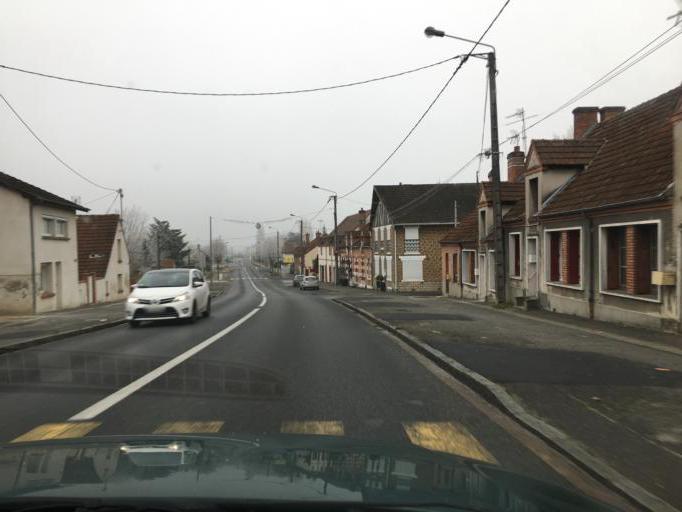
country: FR
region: Centre
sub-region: Departement du Loiret
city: La Ferte-Saint-Aubin
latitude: 47.7096
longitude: 1.9414
